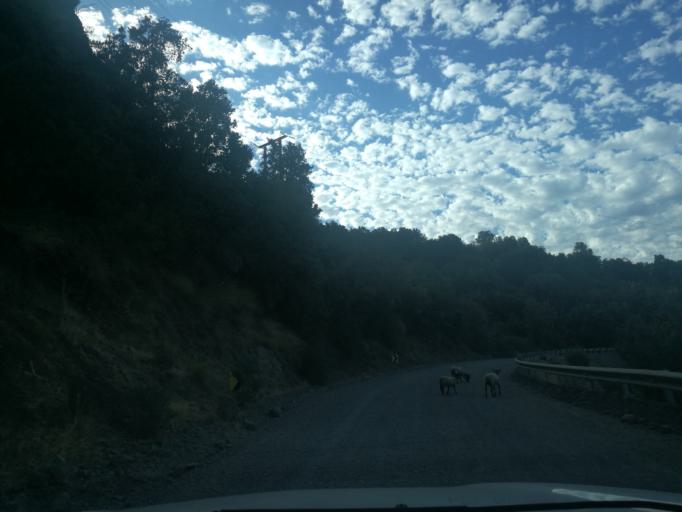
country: CL
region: O'Higgins
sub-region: Provincia de Cachapoal
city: Machali
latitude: -34.2494
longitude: -70.4665
